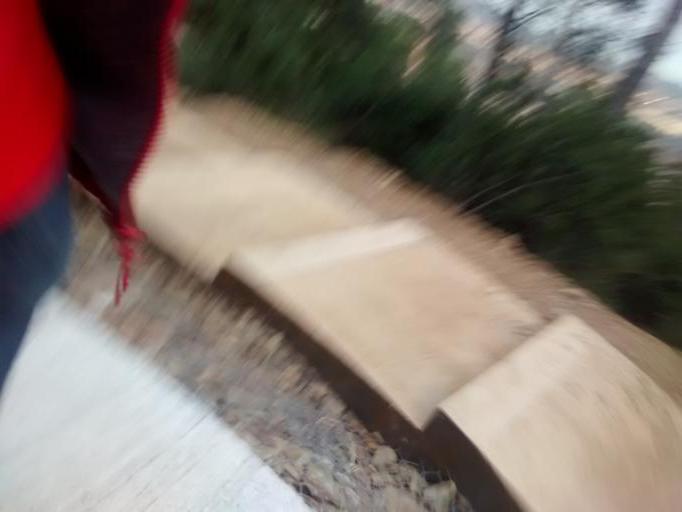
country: ES
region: Catalonia
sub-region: Provincia de Barcelona
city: Sant Vicenc dels Horts
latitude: 41.3964
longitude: 2.0040
